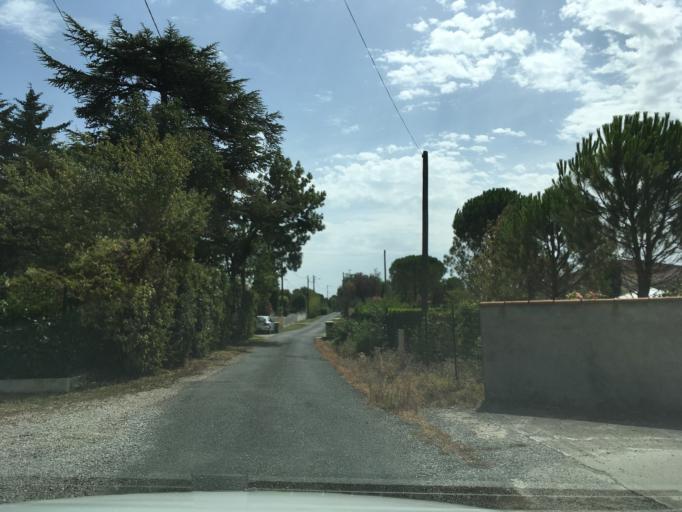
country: FR
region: Midi-Pyrenees
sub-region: Departement du Tarn
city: Castres
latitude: 43.6154
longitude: 2.2171
